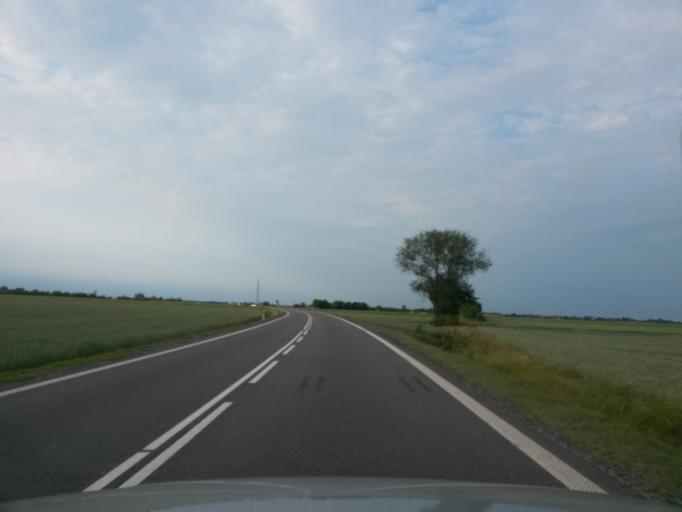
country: PL
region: Lower Silesian Voivodeship
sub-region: Powiat sredzki
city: Ciechow
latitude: 51.0266
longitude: 16.5785
